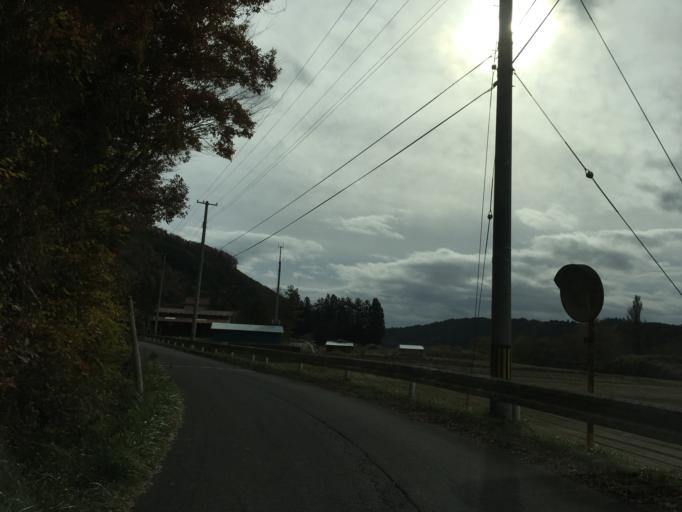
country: JP
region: Iwate
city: Ichinoseki
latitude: 38.7830
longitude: 141.2659
